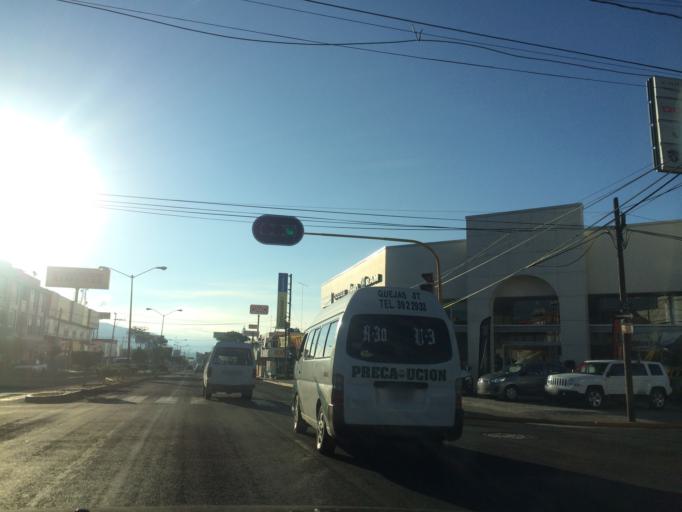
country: MX
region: Puebla
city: Tehuacan
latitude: 18.4635
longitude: -97.4064
